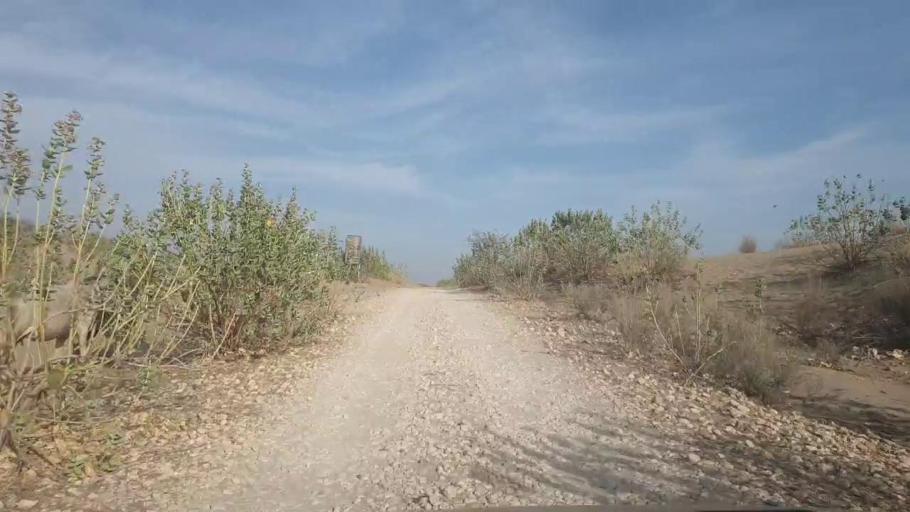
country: PK
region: Sindh
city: Nabisar
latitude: 25.0523
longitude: 69.7220
